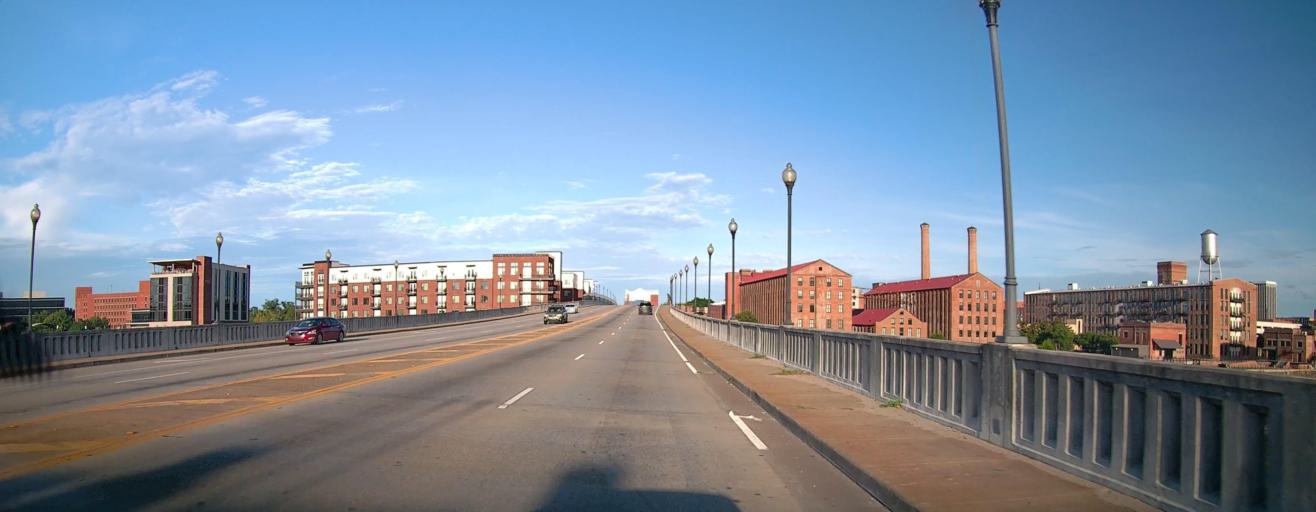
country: US
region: Alabama
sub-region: Russell County
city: Phenix City
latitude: 32.4708
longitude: -84.9979
